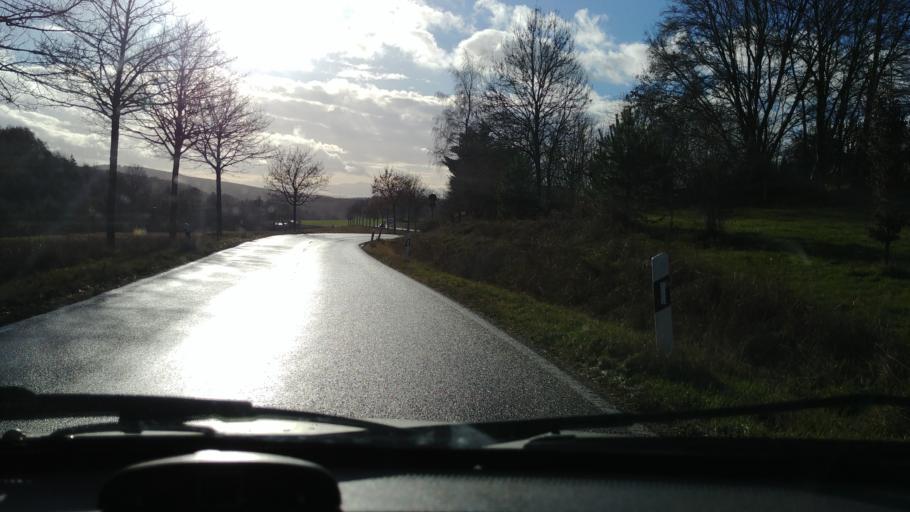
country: DE
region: Hesse
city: Taunusstein
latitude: 50.1797
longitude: 8.1871
